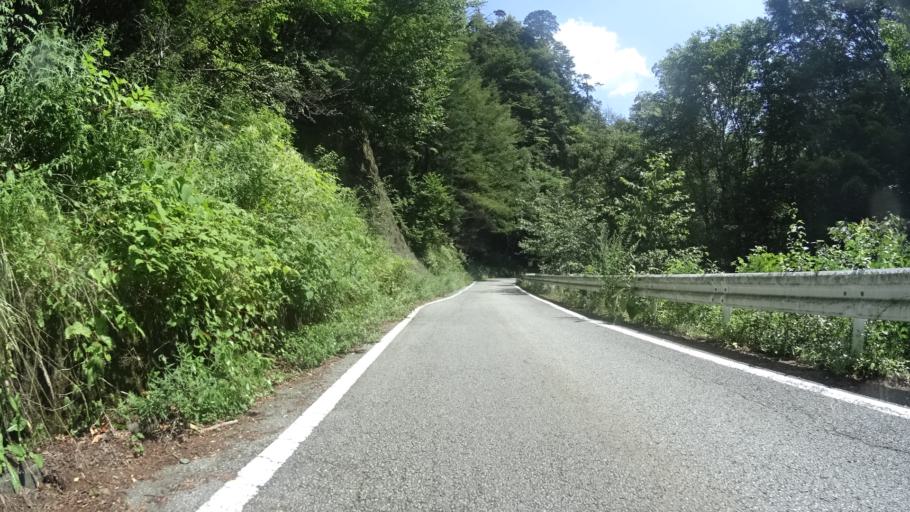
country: JP
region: Yamanashi
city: Enzan
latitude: 35.8181
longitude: 138.6542
